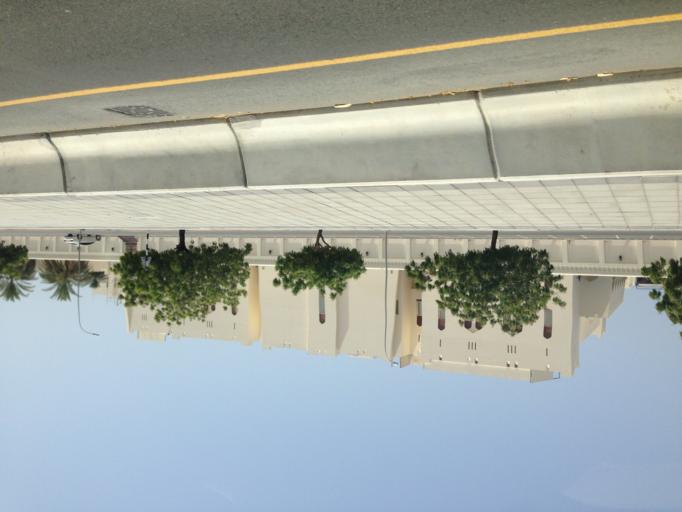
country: OM
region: Muhafazat Masqat
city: Bawshar
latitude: 23.6042
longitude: 58.3284
